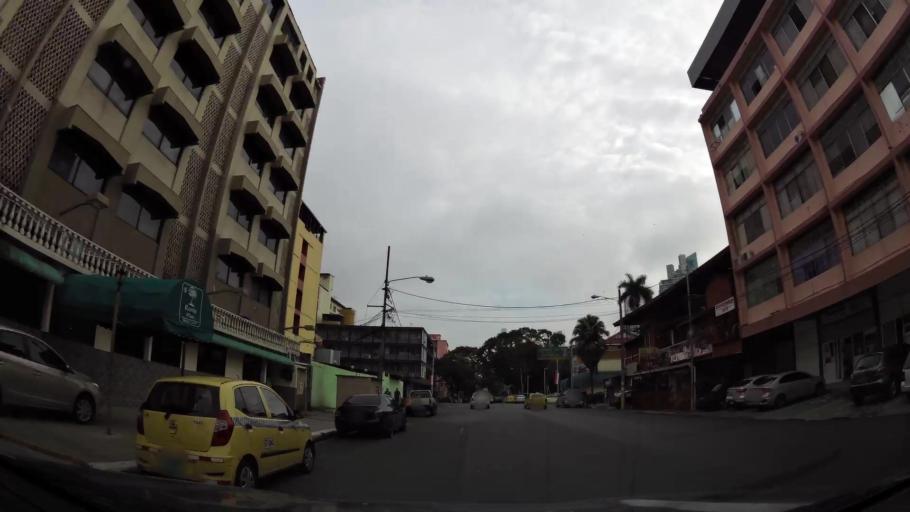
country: PA
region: Panama
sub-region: Distrito de Panama
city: Ancon
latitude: 8.9686
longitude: -79.5352
